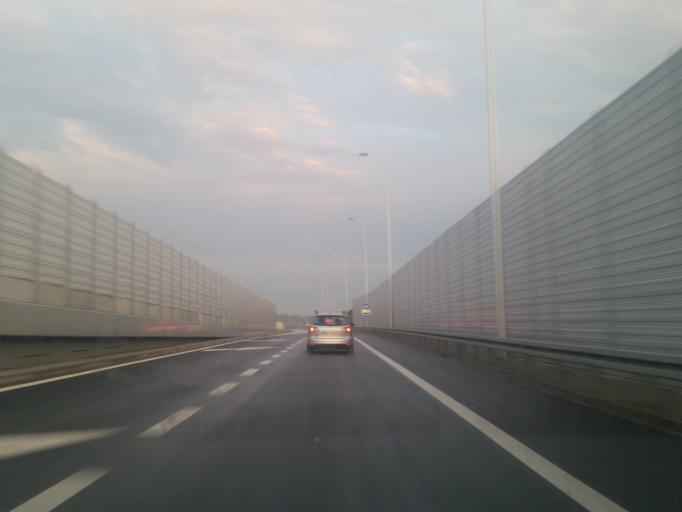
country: PL
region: Masovian Voivodeship
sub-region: Powiat pruszkowski
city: Rybie
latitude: 52.1651
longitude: 20.9378
